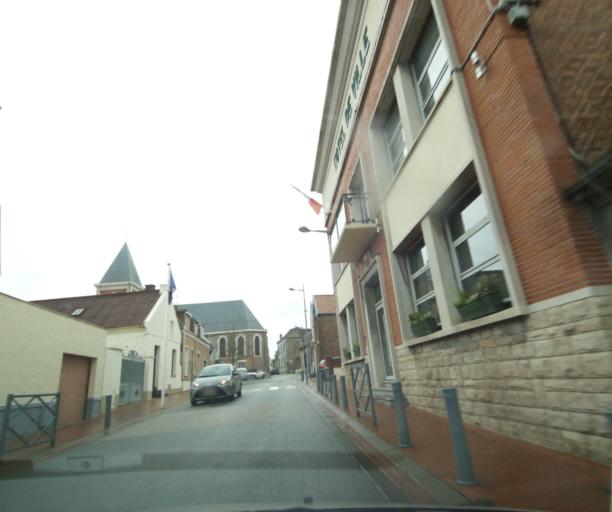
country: FR
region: Nord-Pas-de-Calais
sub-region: Departement du Nord
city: Prouvy
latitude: 50.3181
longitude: 3.4498
